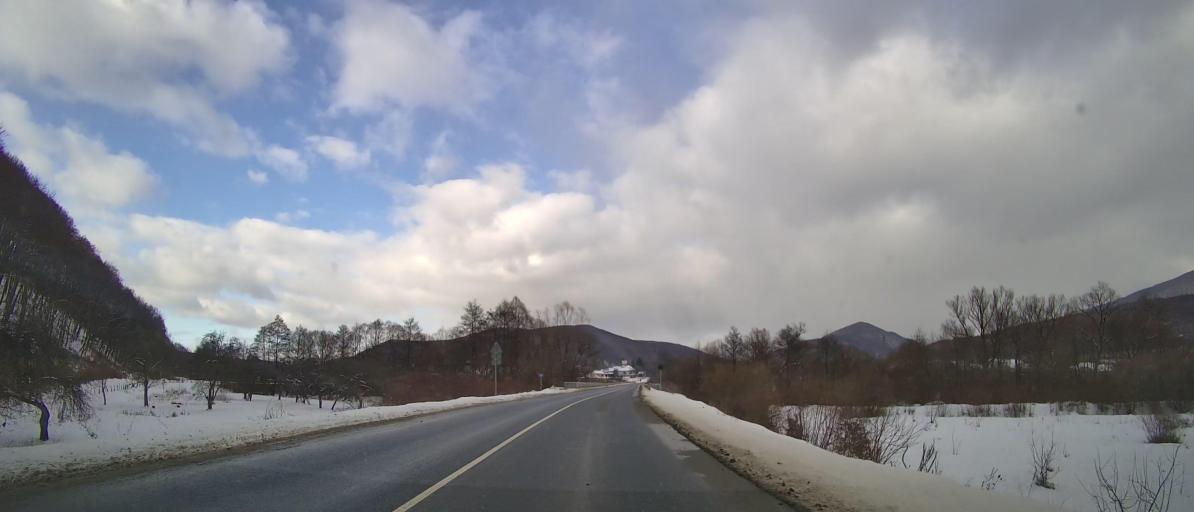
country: UA
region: Zakarpattia
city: Velykyi Bereznyi
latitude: 48.9217
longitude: 22.4555
